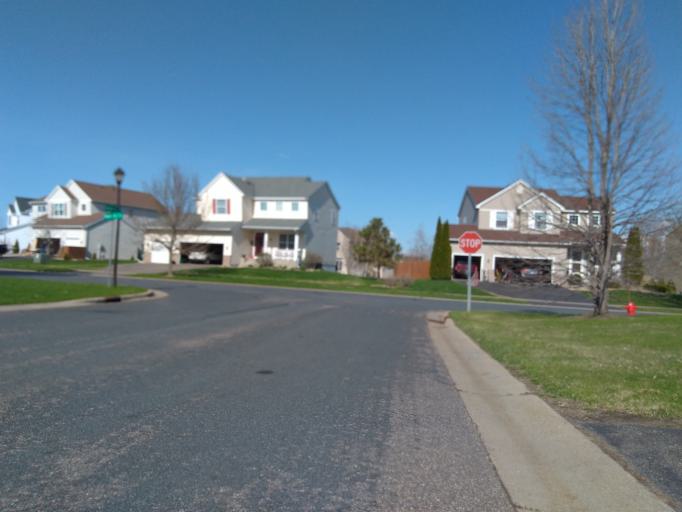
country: US
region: Minnesota
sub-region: Dakota County
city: Rosemount
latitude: 44.7405
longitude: -93.1077
